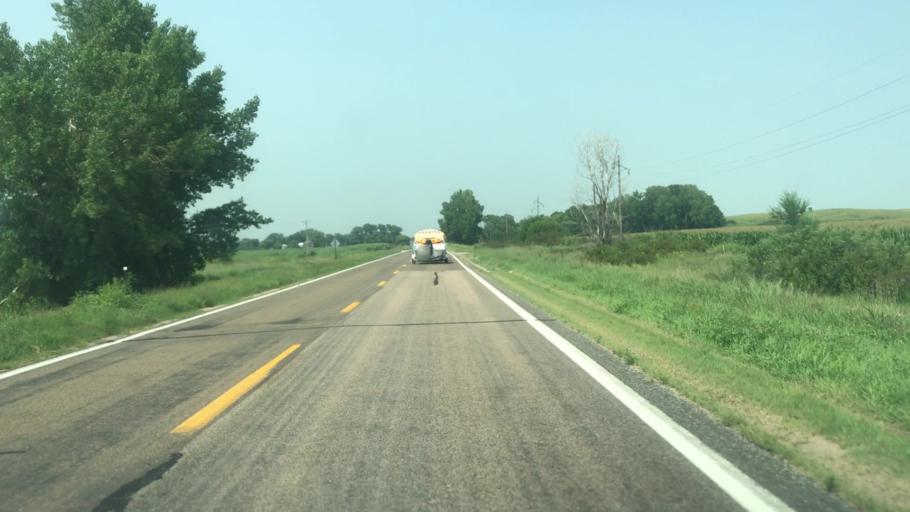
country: US
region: Nebraska
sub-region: Sherman County
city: Loup City
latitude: 41.2382
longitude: -98.9385
